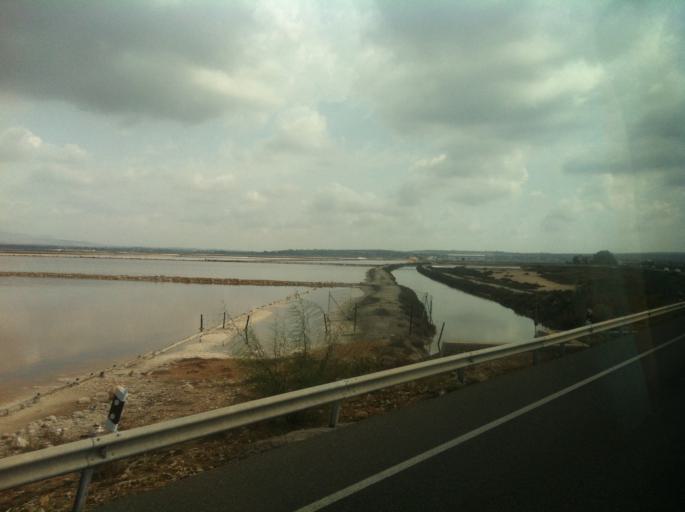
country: ES
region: Valencia
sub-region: Provincia de Alicante
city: Santa Pola
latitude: 38.1857
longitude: -0.6047
